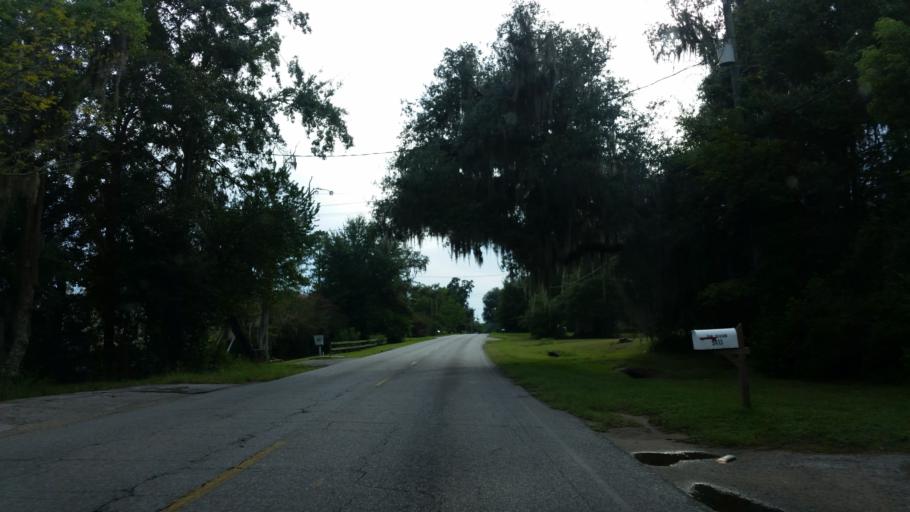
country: US
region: Florida
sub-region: Santa Rosa County
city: Milton
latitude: 30.6358
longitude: -87.0315
